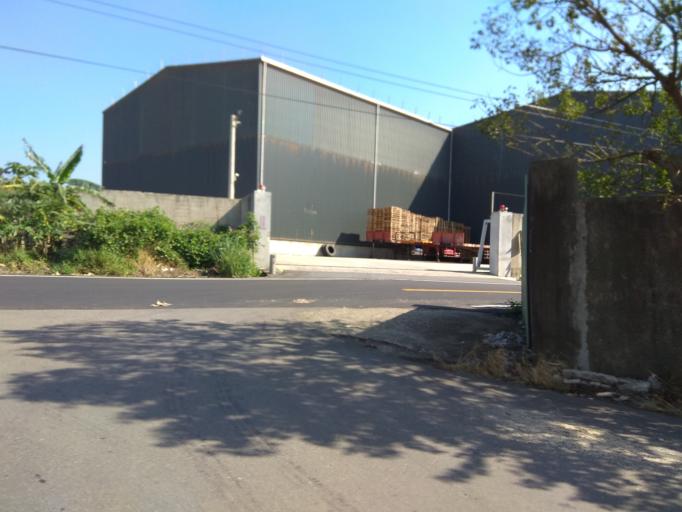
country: TW
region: Taiwan
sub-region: Hsinchu
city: Zhubei
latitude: 24.9840
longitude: 121.0361
